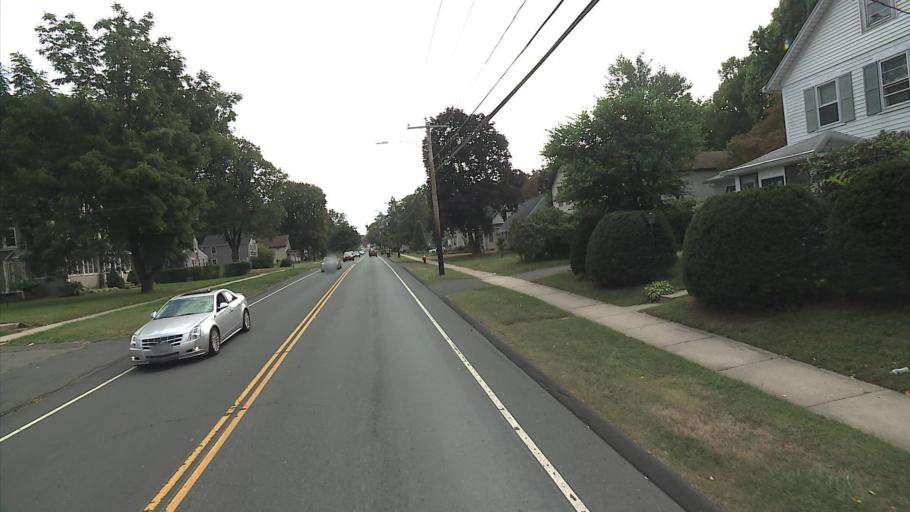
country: US
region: Connecticut
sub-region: Hartford County
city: Newington
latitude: 41.7016
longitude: -72.7248
